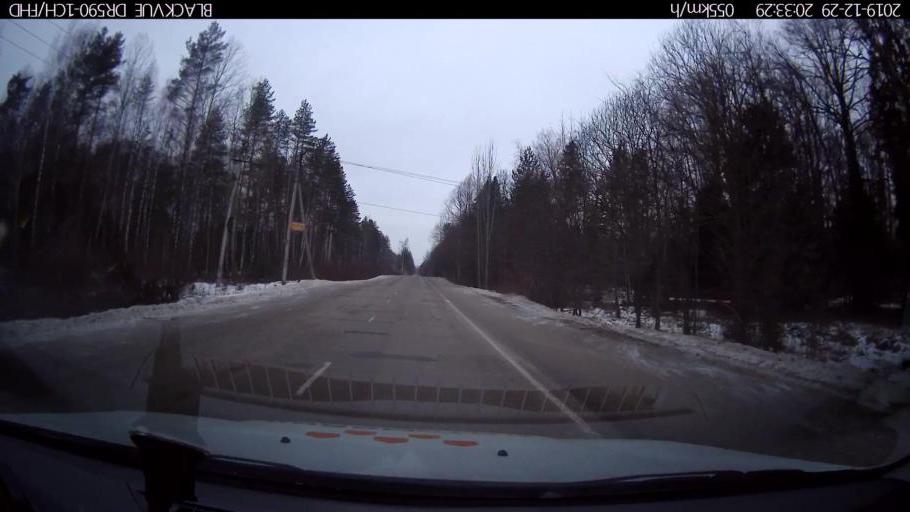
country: RU
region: Nizjnij Novgorod
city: Afonino
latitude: 56.1807
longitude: 44.0515
